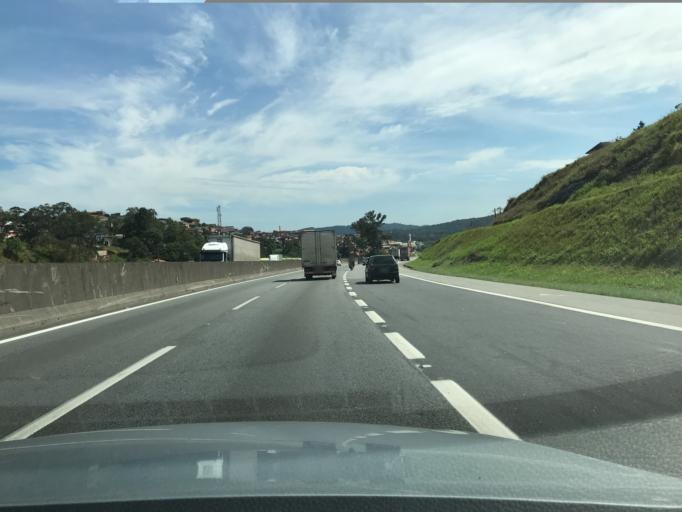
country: BR
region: Sao Paulo
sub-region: Osasco
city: Osasco
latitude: -23.4483
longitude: -46.7873
